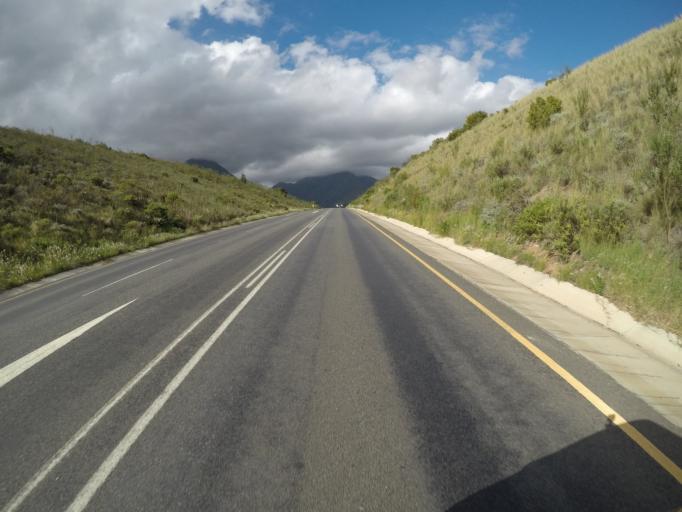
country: ZA
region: Western Cape
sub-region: Overberg District Municipality
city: Swellendam
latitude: -33.9954
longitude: 20.3446
